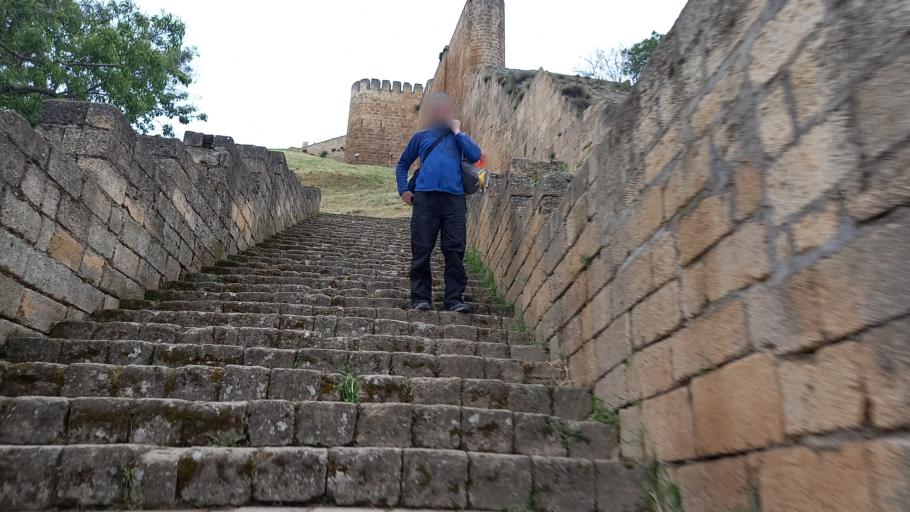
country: RU
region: Dagestan
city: Derbent
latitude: 42.0530
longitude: 48.2763
